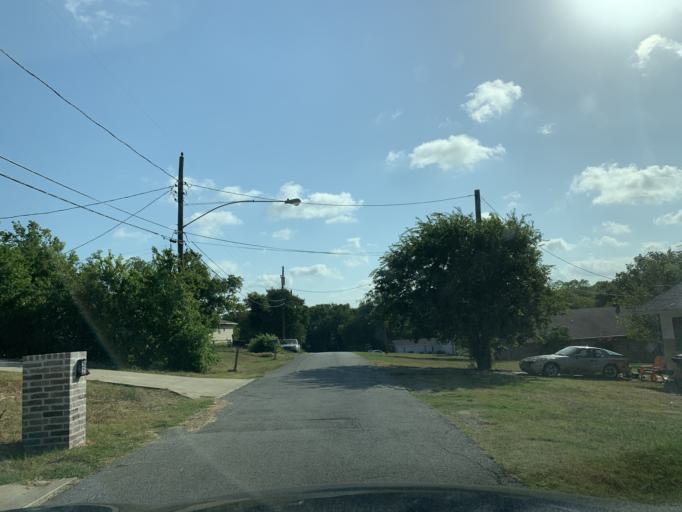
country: US
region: Texas
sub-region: Dallas County
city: Hutchins
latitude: 32.6746
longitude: -96.7751
